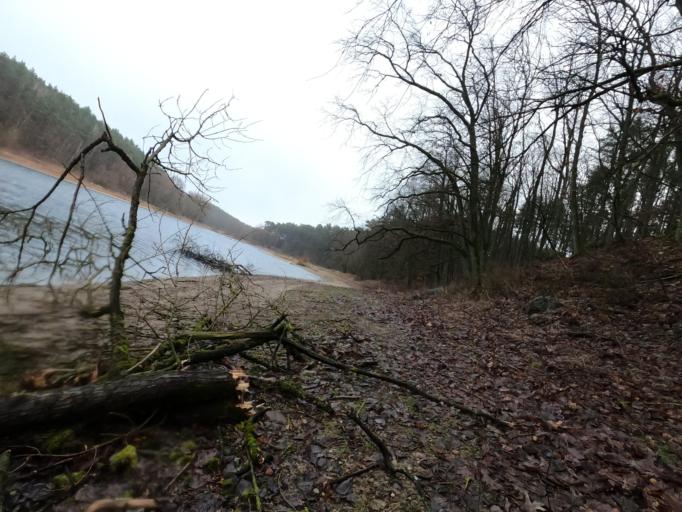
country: PL
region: Greater Poland Voivodeship
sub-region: Powiat pilski
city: Kaczory
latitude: 53.1108
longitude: 16.9070
